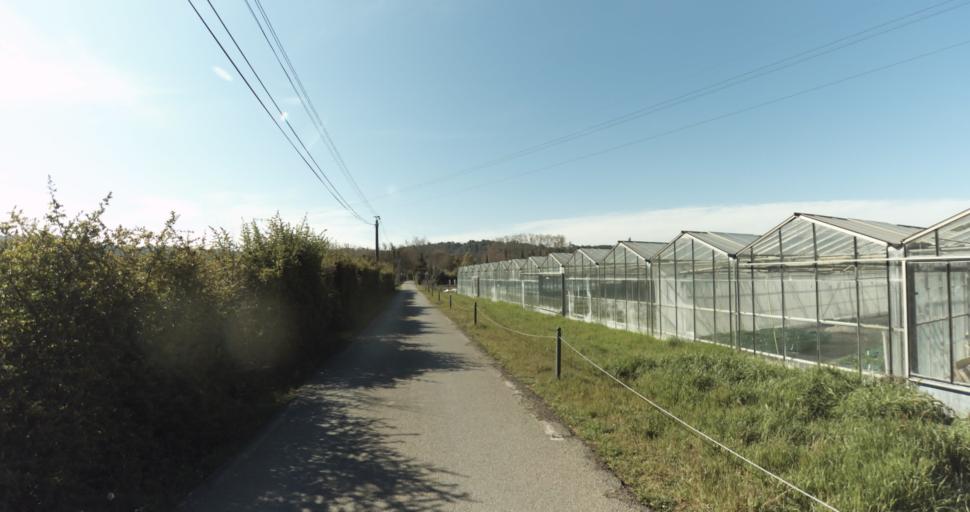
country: FR
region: Provence-Alpes-Cote d'Azur
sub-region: Departement des Bouches-du-Rhone
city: Aix-en-Provence
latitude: 43.5135
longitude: 5.4306
